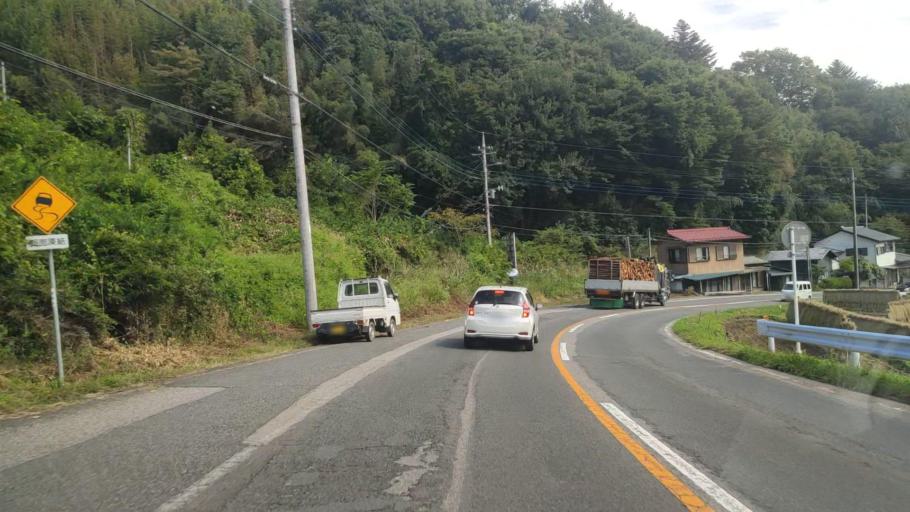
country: JP
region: Gunma
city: Numata
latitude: 36.6279
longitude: 139.0154
